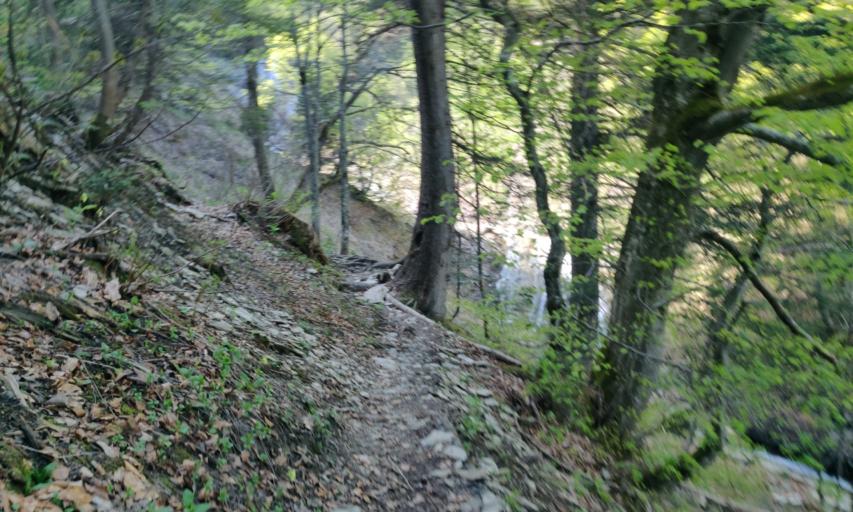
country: CH
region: Saint Gallen
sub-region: Wahlkreis Sarganserland
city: Sargans
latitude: 47.0746
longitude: 9.4413
